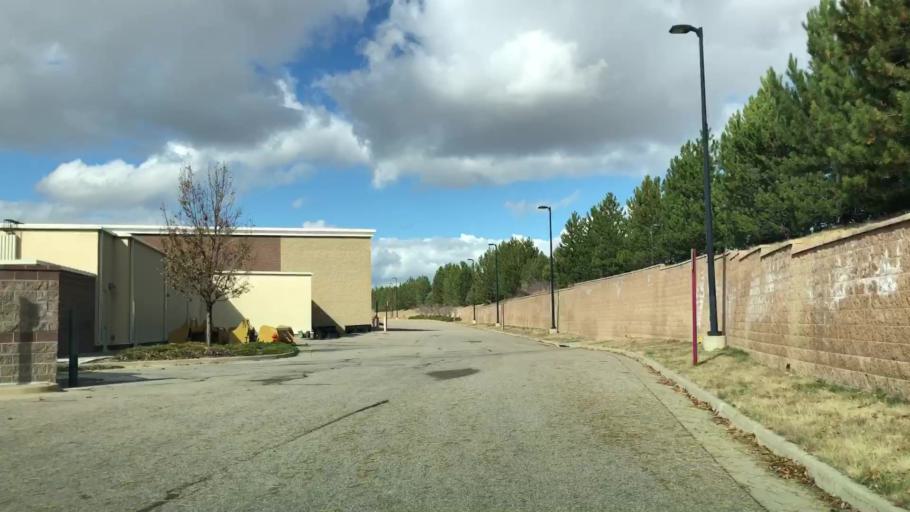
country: US
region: Colorado
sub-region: Larimer County
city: Loveland
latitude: 40.4190
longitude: -104.9886
